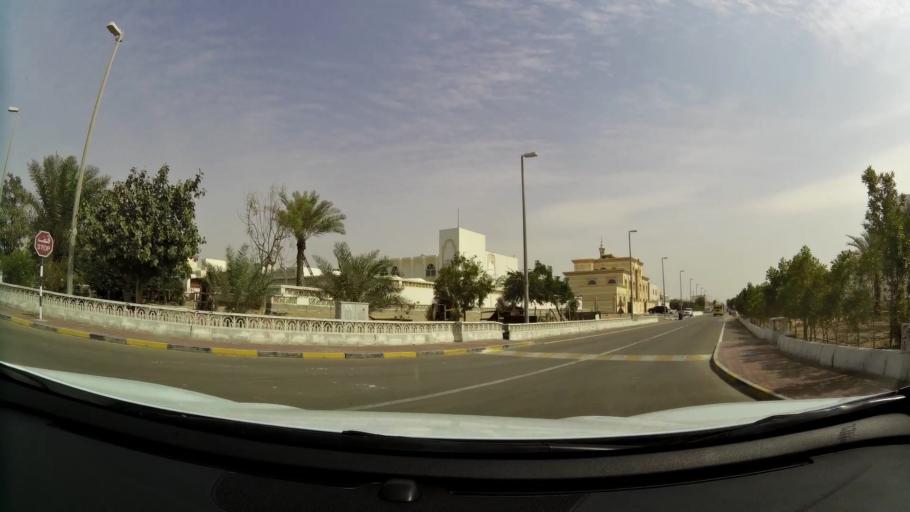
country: AE
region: Abu Dhabi
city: Abu Dhabi
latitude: 24.5466
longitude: 54.6622
